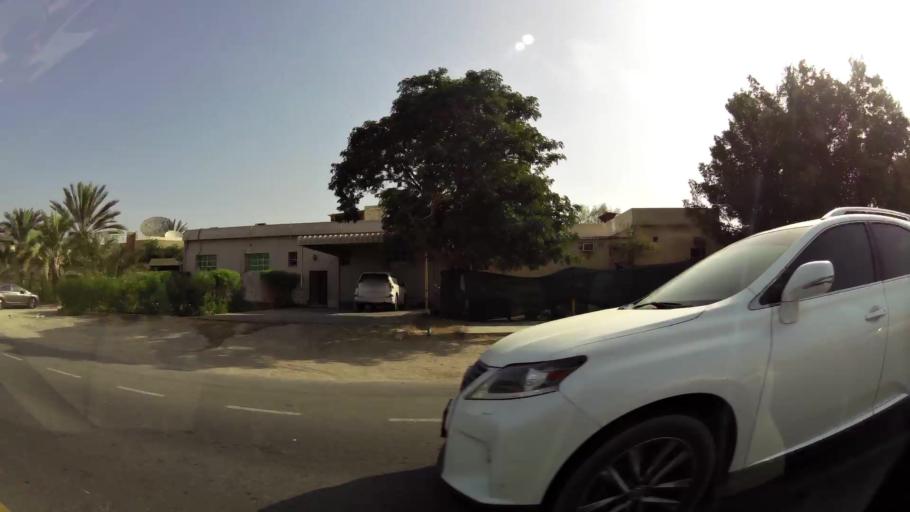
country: AE
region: Ash Shariqah
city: Sharjah
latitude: 25.2192
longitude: 55.3852
